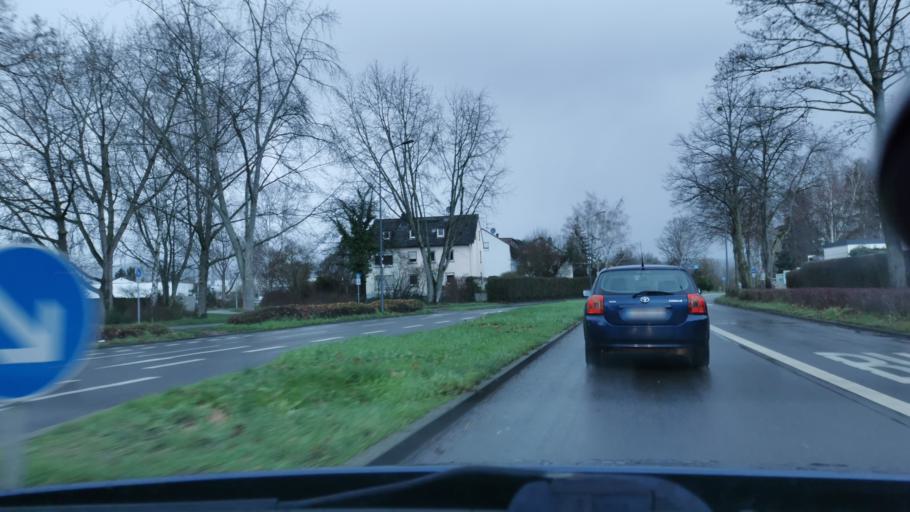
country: DE
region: Rheinland-Pfalz
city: Trier
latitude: 49.7423
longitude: 6.6452
